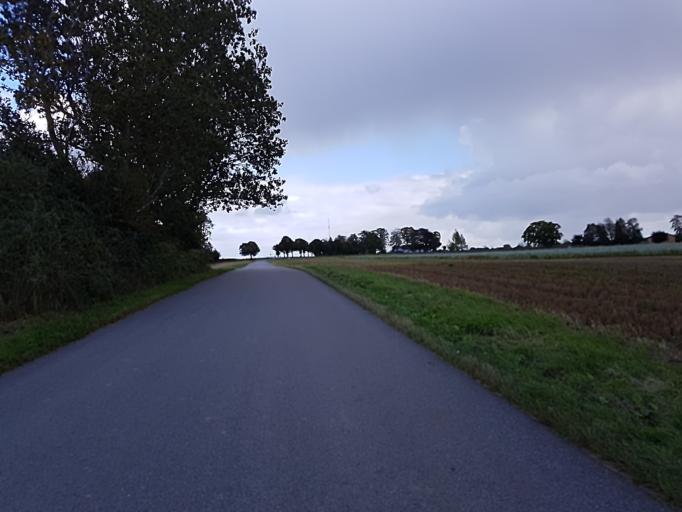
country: DK
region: Zealand
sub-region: Roskilde Kommune
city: Gundsomagle
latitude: 55.7208
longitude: 12.1866
